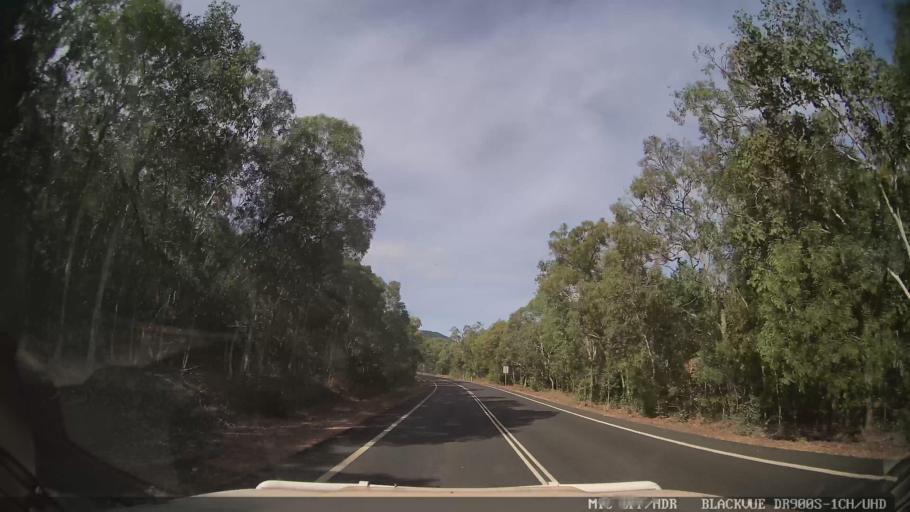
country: AU
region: Queensland
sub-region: Cook
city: Cooktown
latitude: -15.5016
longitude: 145.2402
